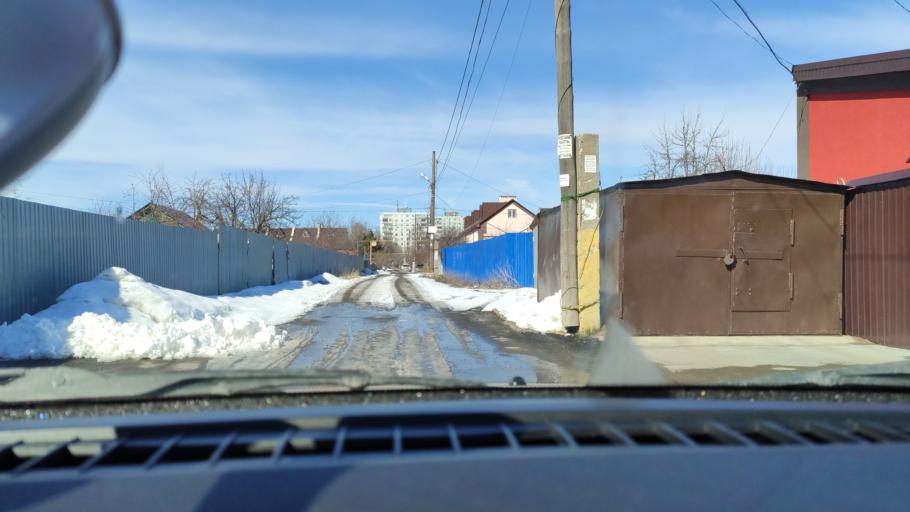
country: RU
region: Samara
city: Samara
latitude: 53.2333
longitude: 50.2379
